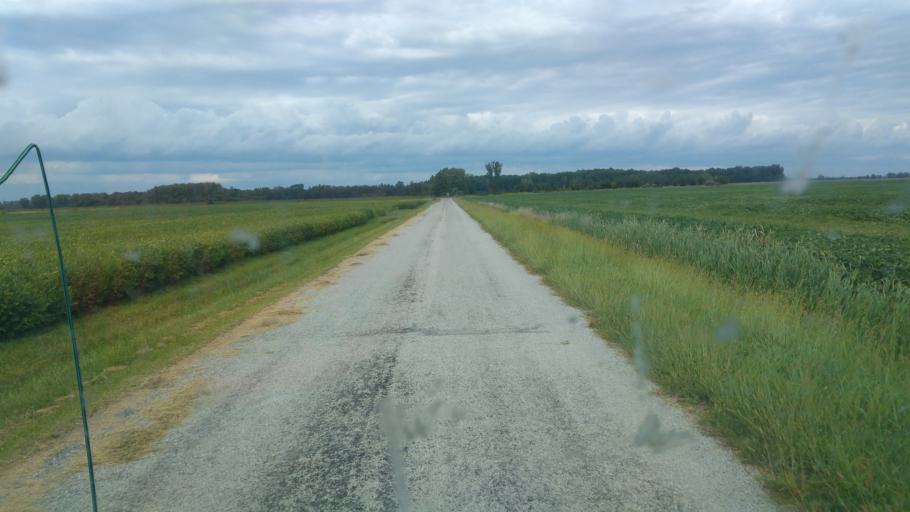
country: US
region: Ohio
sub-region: Wyandot County
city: Upper Sandusky
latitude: 40.6985
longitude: -83.2655
